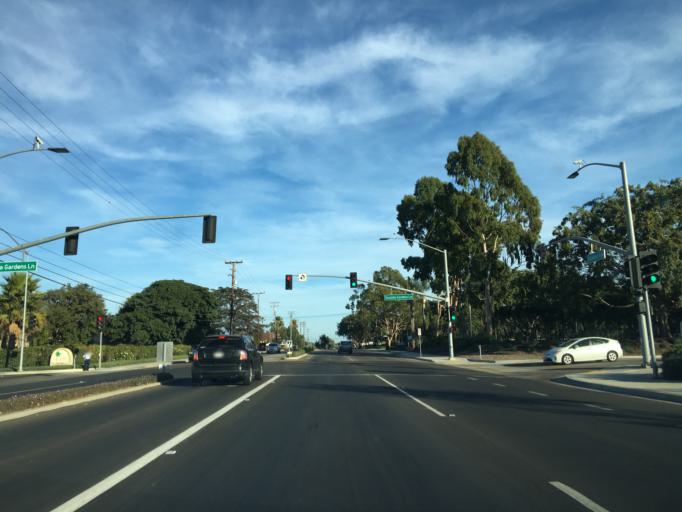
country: US
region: California
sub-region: Santa Barbara County
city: Goleta
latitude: 34.4352
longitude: -119.8146
